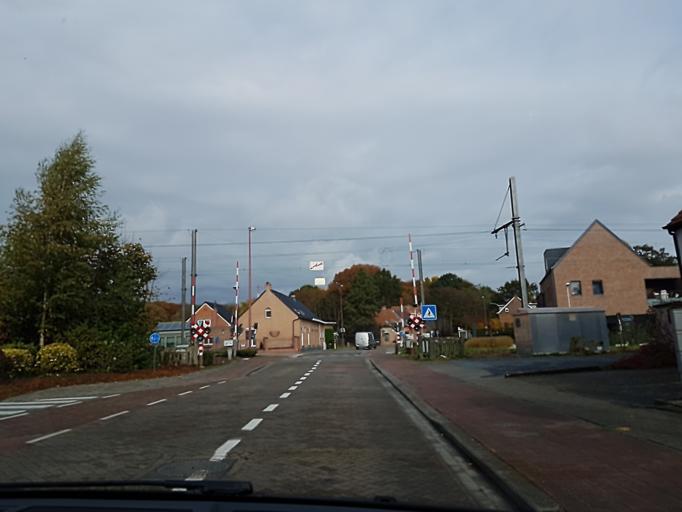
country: BE
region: Flanders
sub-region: Provincie Antwerpen
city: Lint
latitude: 51.1295
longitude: 4.4971
